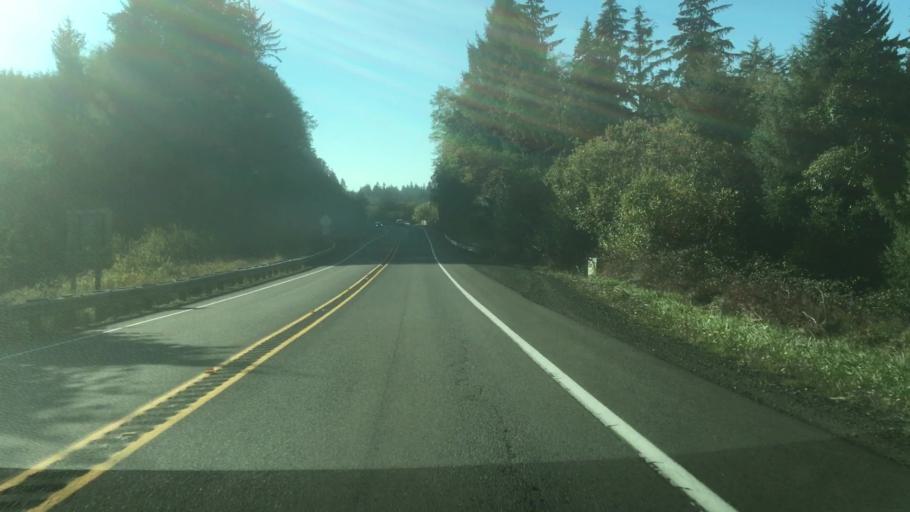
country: US
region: Washington
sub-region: Pacific County
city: South Bend
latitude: 46.6795
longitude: -123.8981
